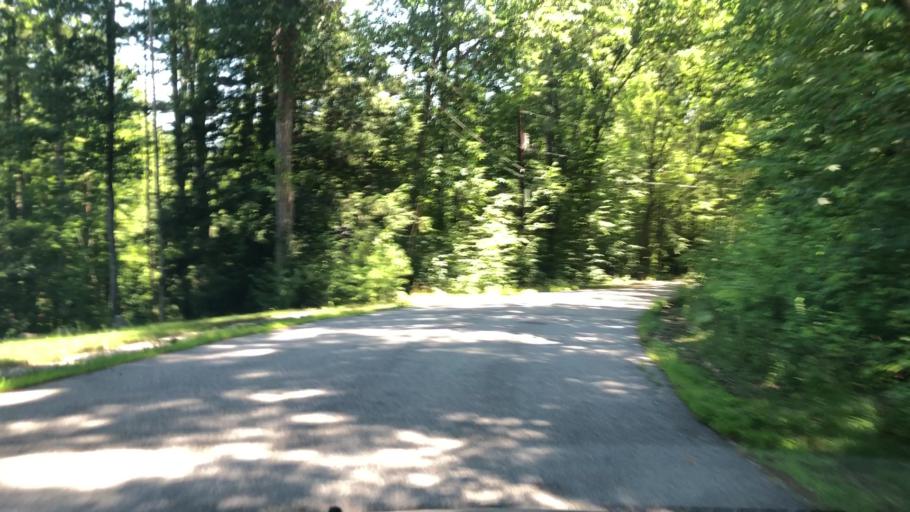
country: US
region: New Hampshire
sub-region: Hillsborough County
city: Milford
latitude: 42.8397
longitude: -71.5787
